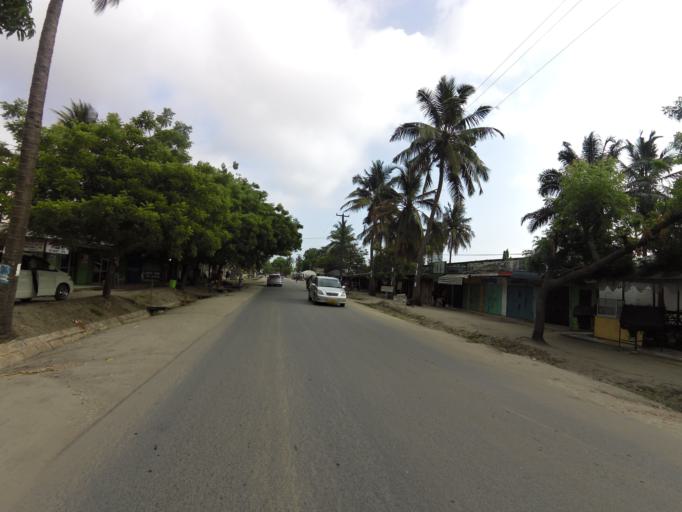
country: TZ
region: Dar es Salaam
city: Magomeni
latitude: -6.7806
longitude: 39.2407
